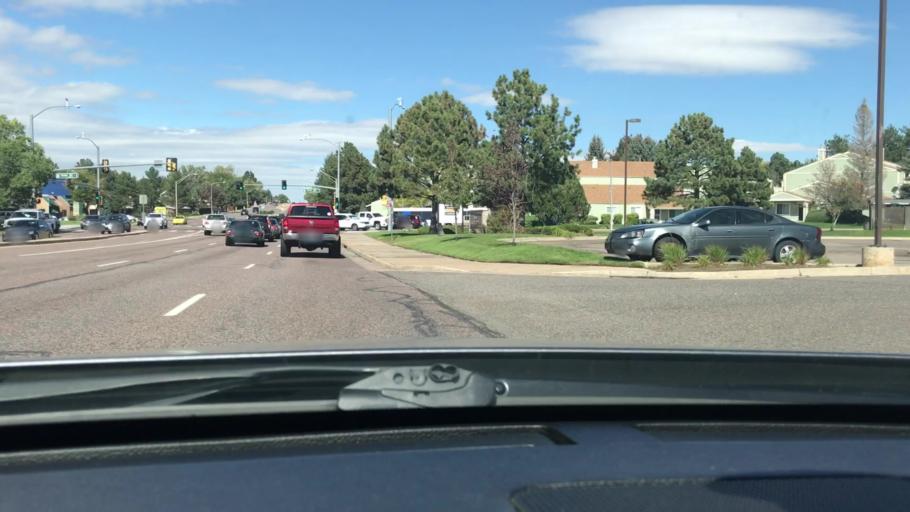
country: US
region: Colorado
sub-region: Arapahoe County
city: Dove Valley
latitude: 39.6317
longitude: -104.8102
